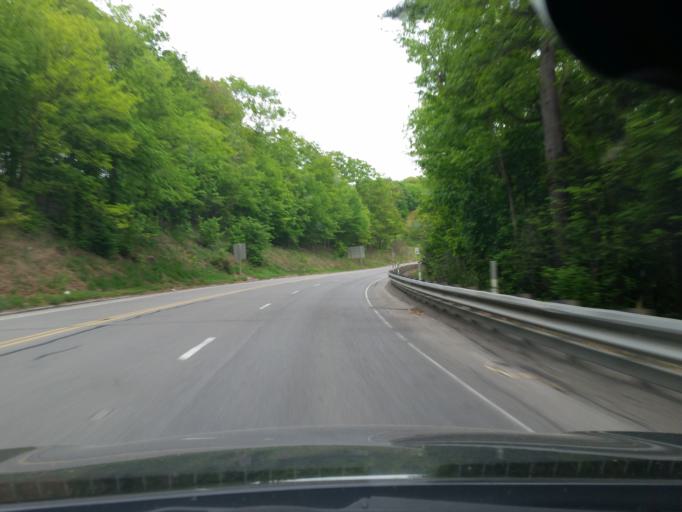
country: US
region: Pennsylvania
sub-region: Elk County
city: Ridgway
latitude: 41.4206
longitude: -78.7178
